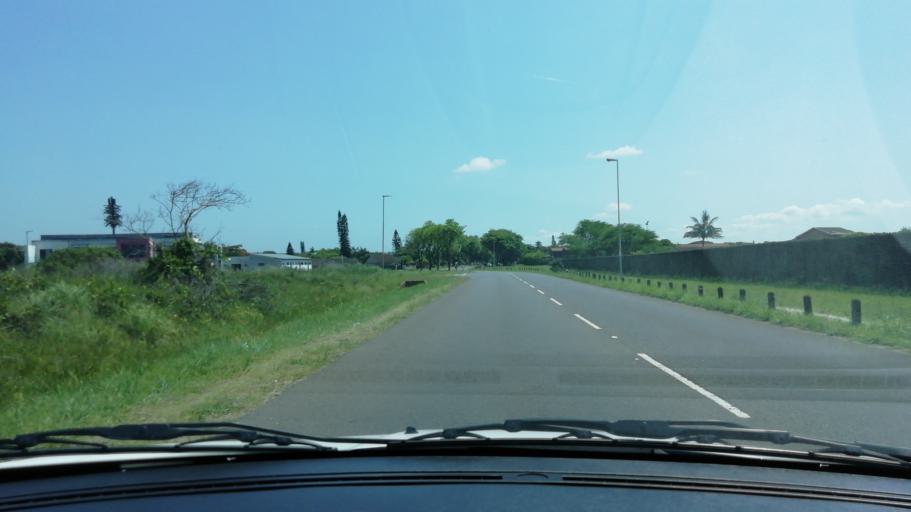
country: ZA
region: KwaZulu-Natal
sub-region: uThungulu District Municipality
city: Richards Bay
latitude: -28.7416
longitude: 32.0525
